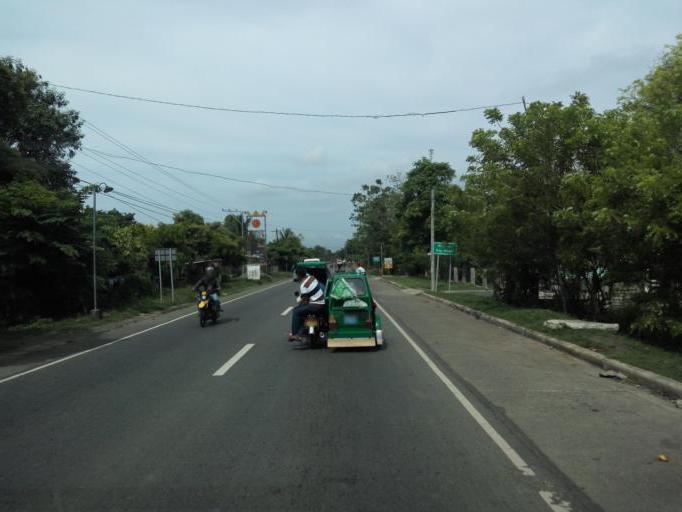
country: PH
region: Cagayan Valley
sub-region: Province of Isabela
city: Reina Mercedes
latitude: 16.9911
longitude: 121.8068
